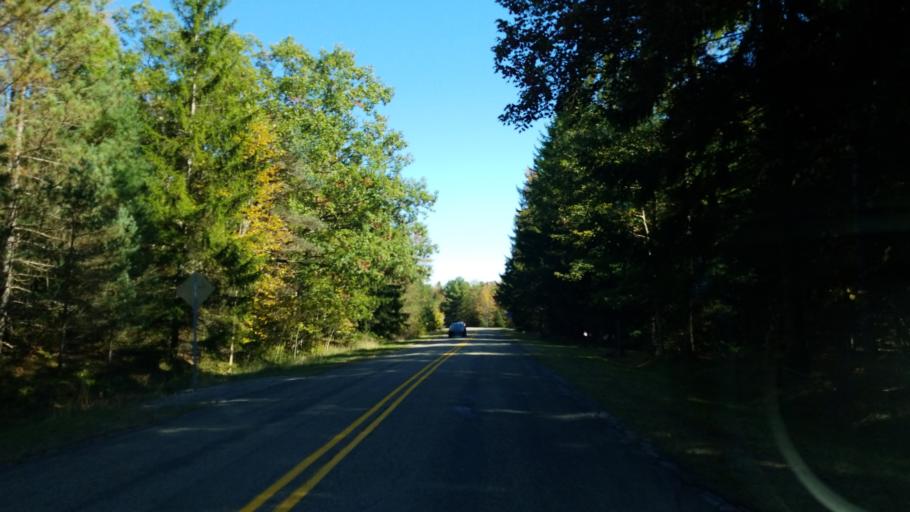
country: US
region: Pennsylvania
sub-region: Clearfield County
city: Shiloh
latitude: 41.2615
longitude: -78.2960
